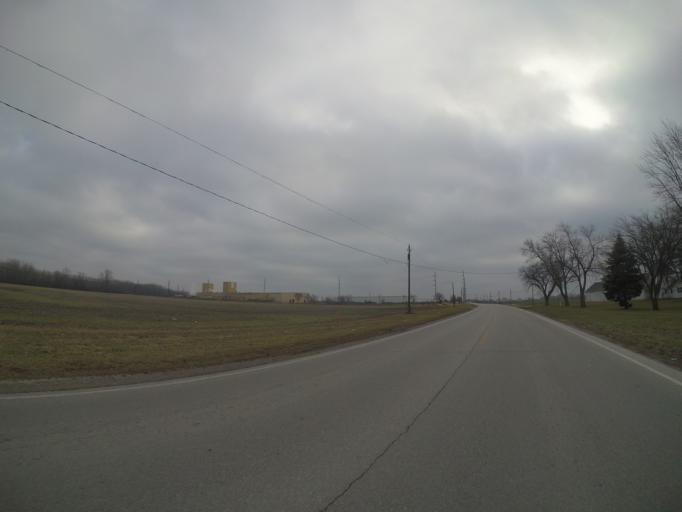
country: US
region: Ohio
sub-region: Wood County
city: Walbridge
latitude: 41.5999
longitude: -83.5127
